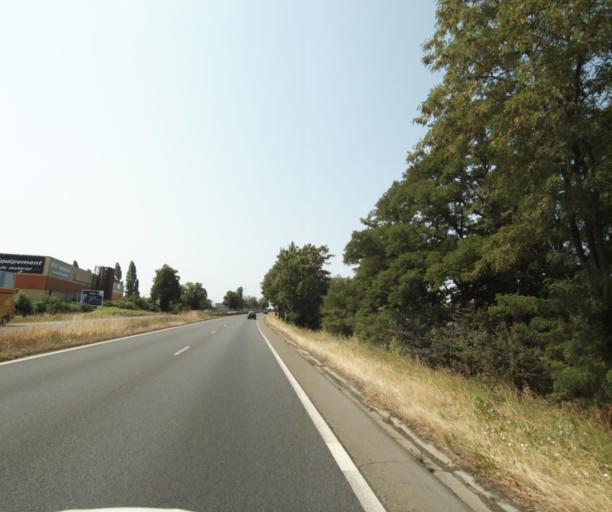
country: FR
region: Ile-de-France
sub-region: Departement du Val-d'Oise
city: Eragny
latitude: 49.0115
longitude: 2.0890
